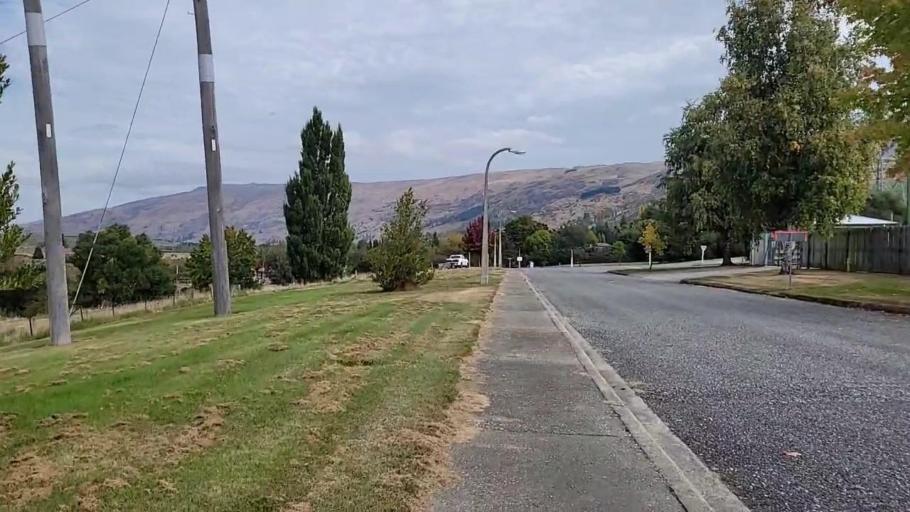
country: NZ
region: Otago
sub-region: Queenstown-Lakes District
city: Kingston
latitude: -45.4771
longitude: 169.3178
